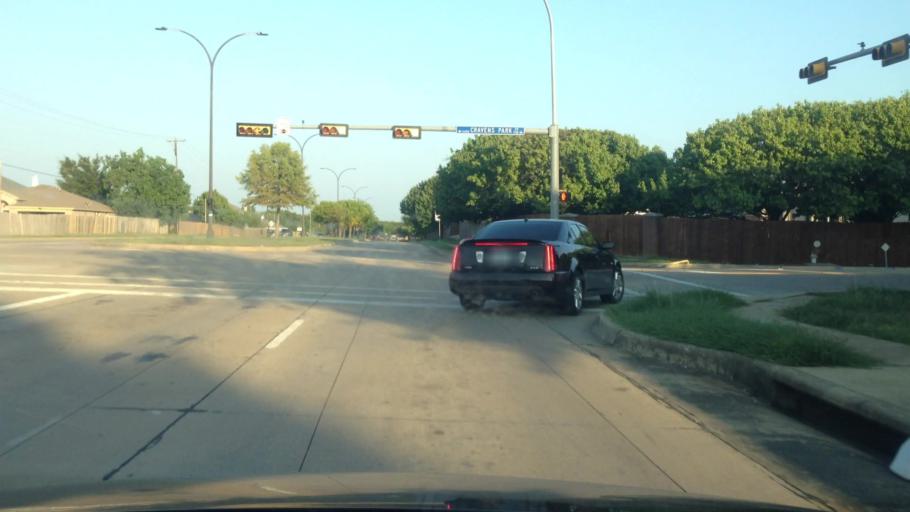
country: US
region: Texas
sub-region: Tarrant County
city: Dalworthington Gardens
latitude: 32.6547
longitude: -97.1000
